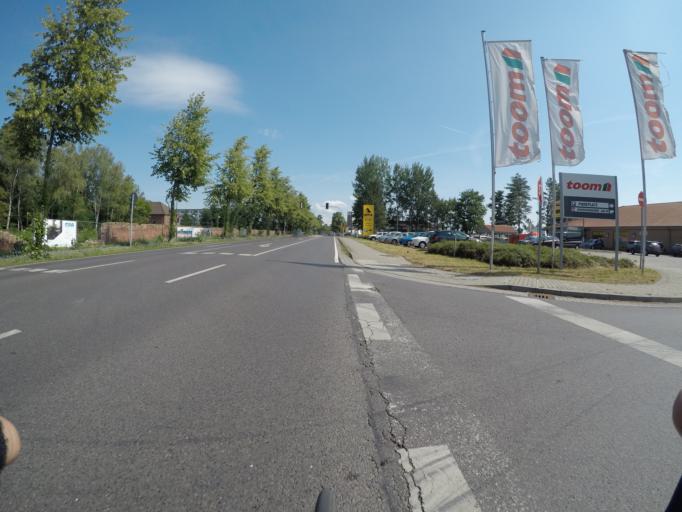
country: DE
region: Brandenburg
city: Bernau bei Berlin
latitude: 52.6672
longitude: 13.5812
